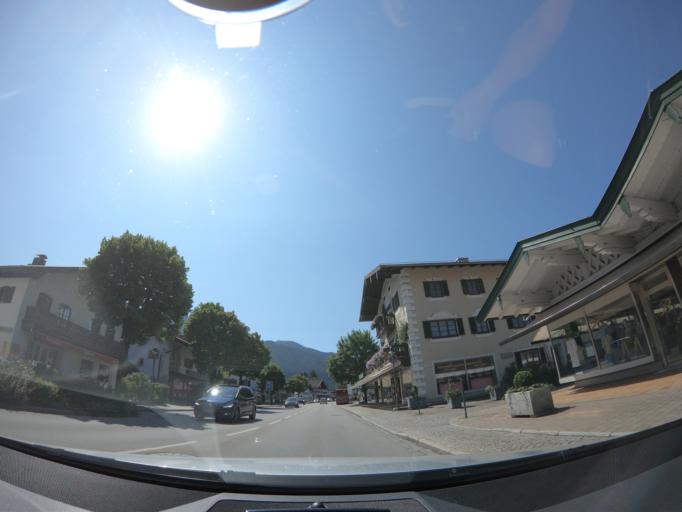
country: DE
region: Bavaria
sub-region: Upper Bavaria
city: Rottach-Egern
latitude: 47.6913
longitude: 11.7706
